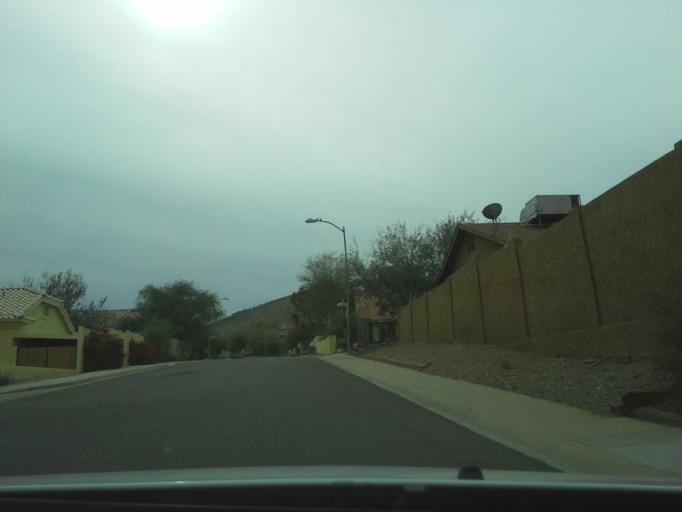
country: US
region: Arizona
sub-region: Maricopa County
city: Paradise Valley
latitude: 33.6201
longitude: -112.0242
